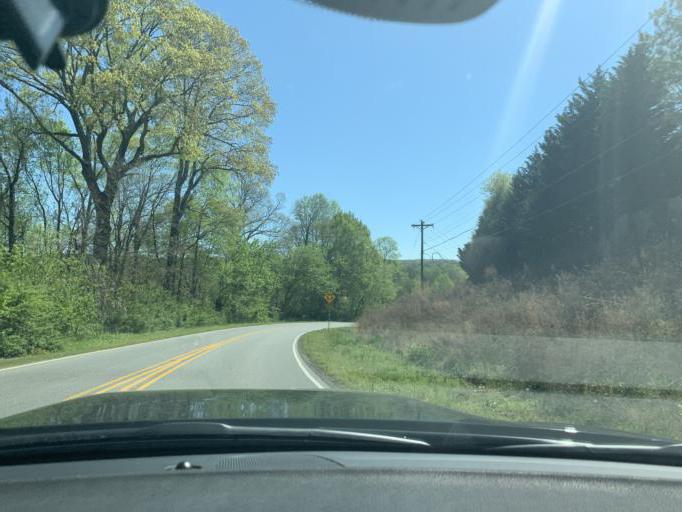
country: US
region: Georgia
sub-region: Fulton County
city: Milton
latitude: 34.1352
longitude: -84.2210
